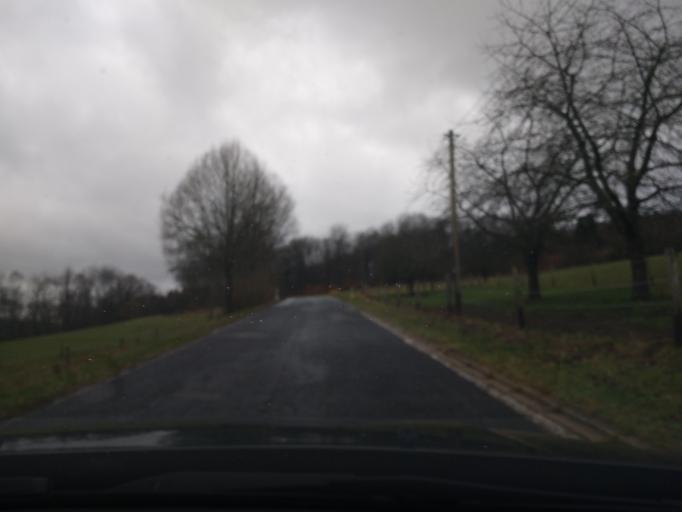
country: DE
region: Rheinland-Pfalz
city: Schomerich
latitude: 49.6333
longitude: 6.7104
